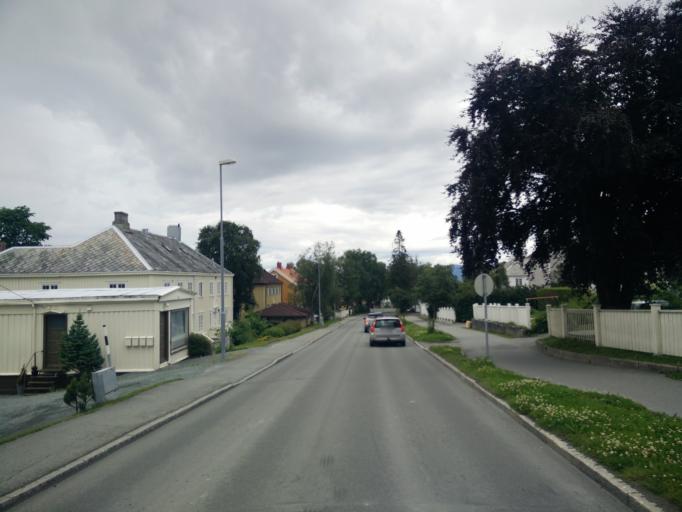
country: NO
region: Sor-Trondelag
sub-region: Trondheim
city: Trondheim
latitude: 63.4188
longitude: 10.4131
